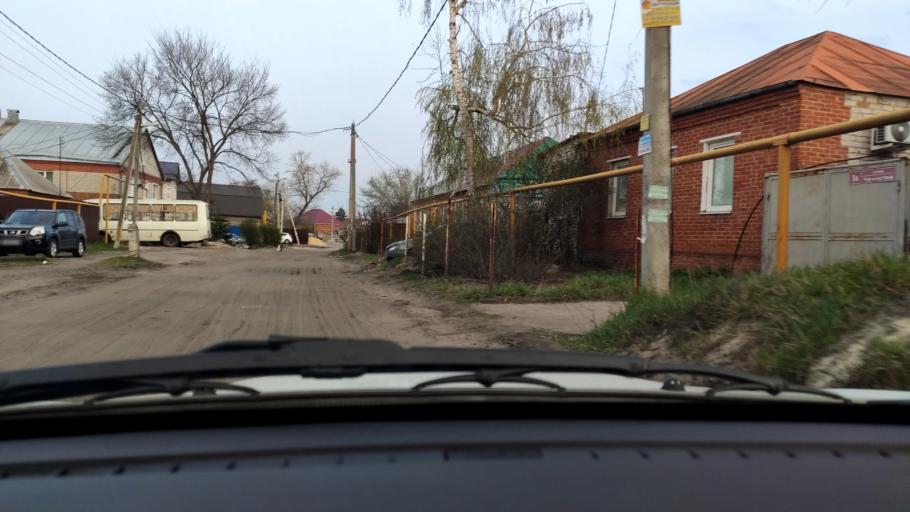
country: RU
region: Voronezj
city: Somovo
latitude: 51.7498
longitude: 39.3347
